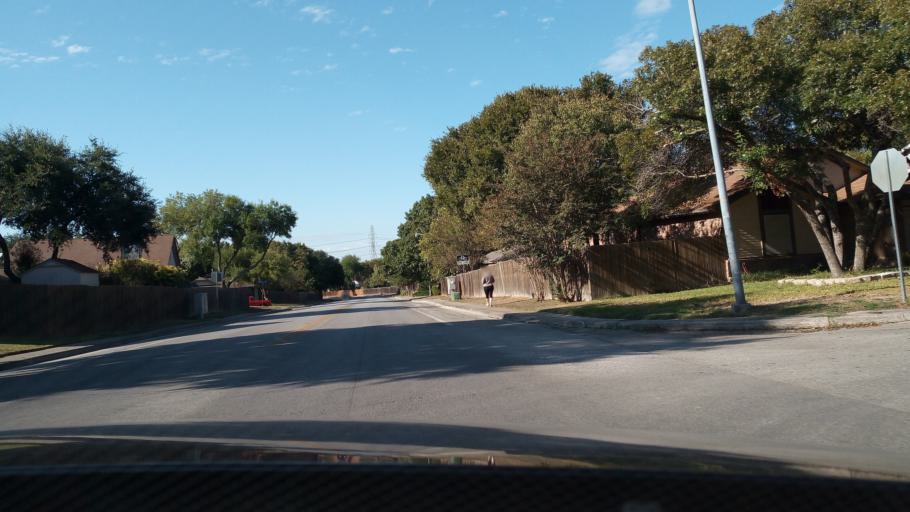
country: US
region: Texas
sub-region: Bexar County
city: Hollywood Park
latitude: 29.5600
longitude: -98.4375
